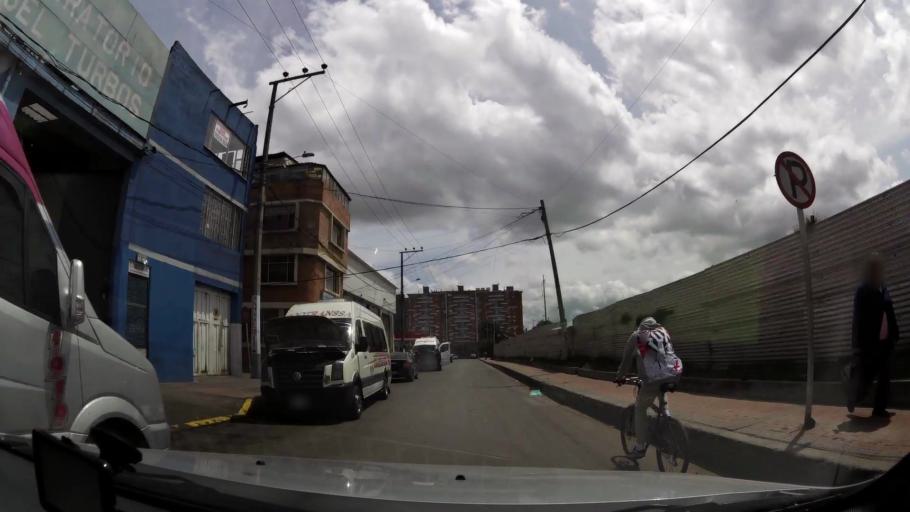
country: CO
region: Bogota D.C.
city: Bogota
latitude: 4.6528
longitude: -74.1316
